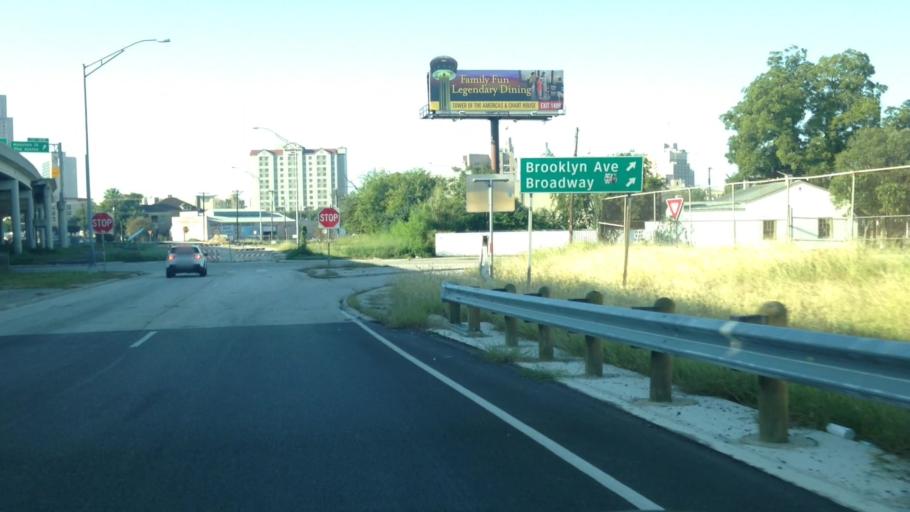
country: US
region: Texas
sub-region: Bexar County
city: San Antonio
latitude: 29.4305
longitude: -98.4810
